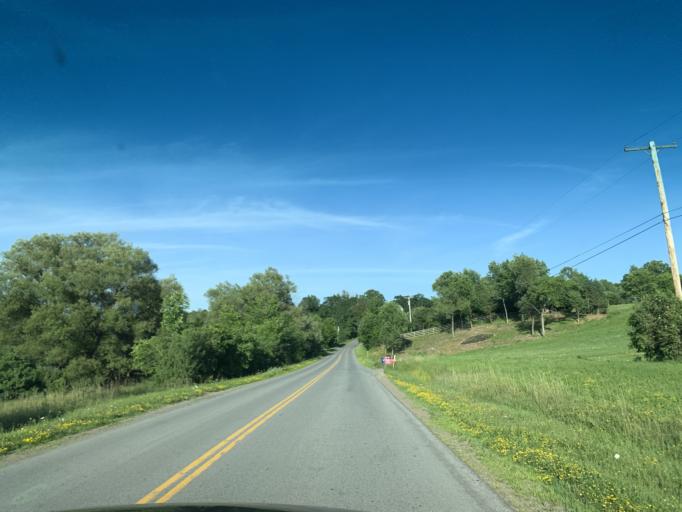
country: US
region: New York
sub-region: Oneida County
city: Vernon
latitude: 43.0560
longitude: -75.4674
